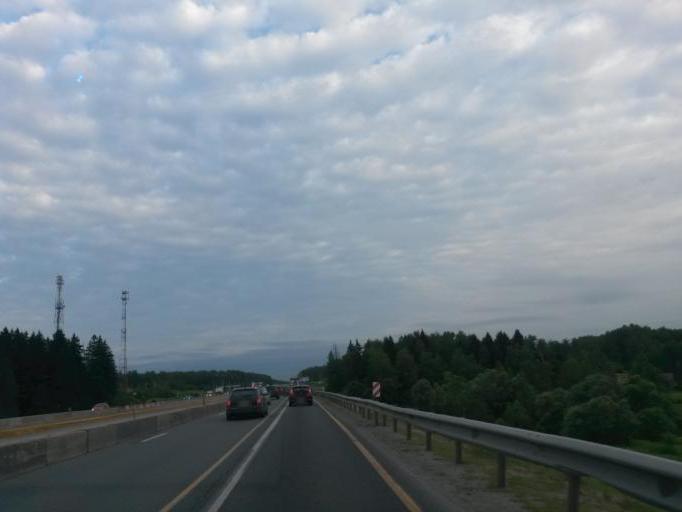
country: RU
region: Moskovskaya
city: Lyubuchany
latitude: 55.2342
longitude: 37.5278
